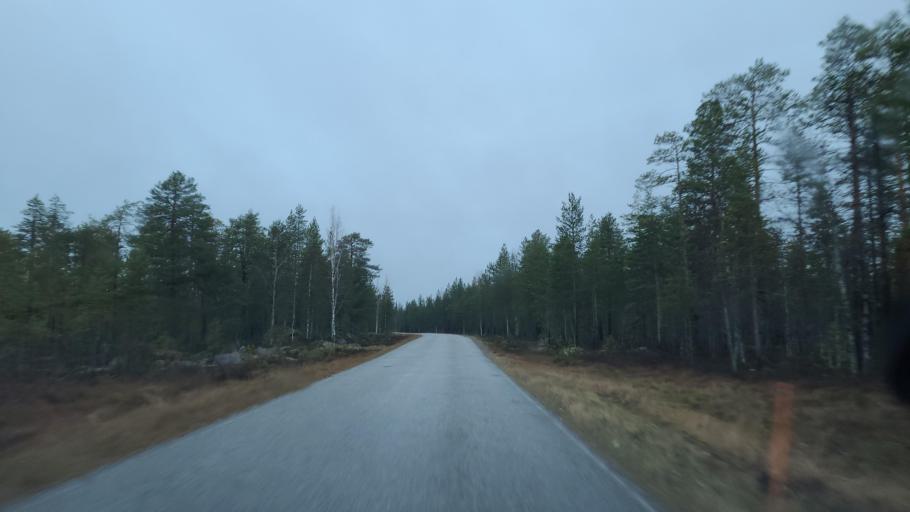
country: FI
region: Lapland
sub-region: Kemi-Tornio
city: Simo
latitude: 65.8840
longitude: 25.2211
